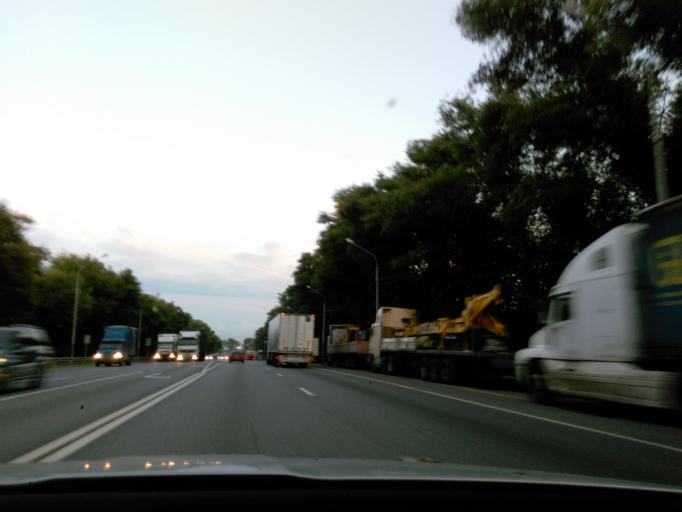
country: RU
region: Moskovskaya
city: Klin
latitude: 56.3638
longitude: 36.6903
